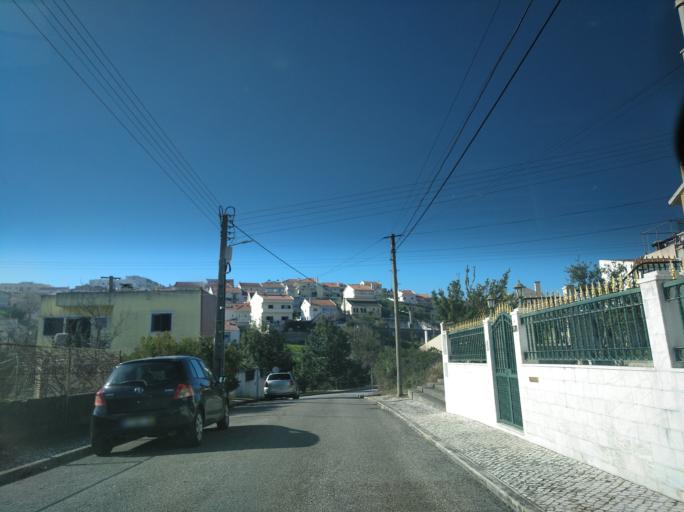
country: PT
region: Lisbon
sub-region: Odivelas
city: Famoes
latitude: 38.7920
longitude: -9.2204
